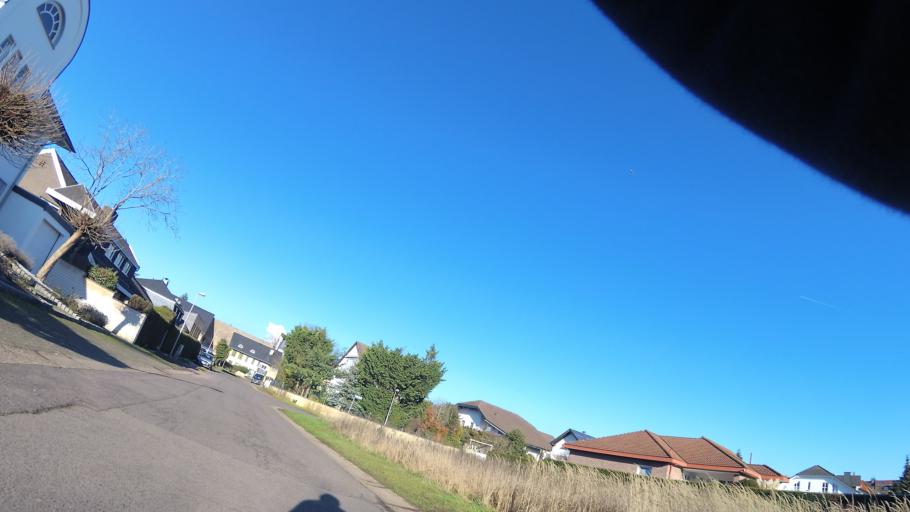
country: DE
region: Saarland
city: Saarlouis
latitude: 49.3082
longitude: 6.7535
